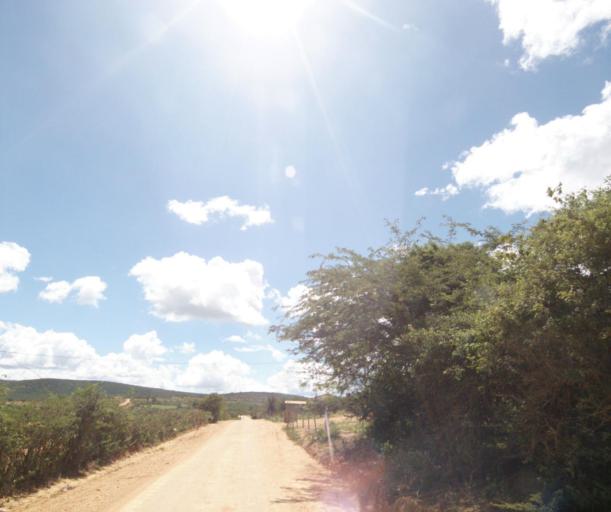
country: BR
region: Bahia
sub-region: Pocoes
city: Pocoes
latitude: -14.2997
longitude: -40.6539
